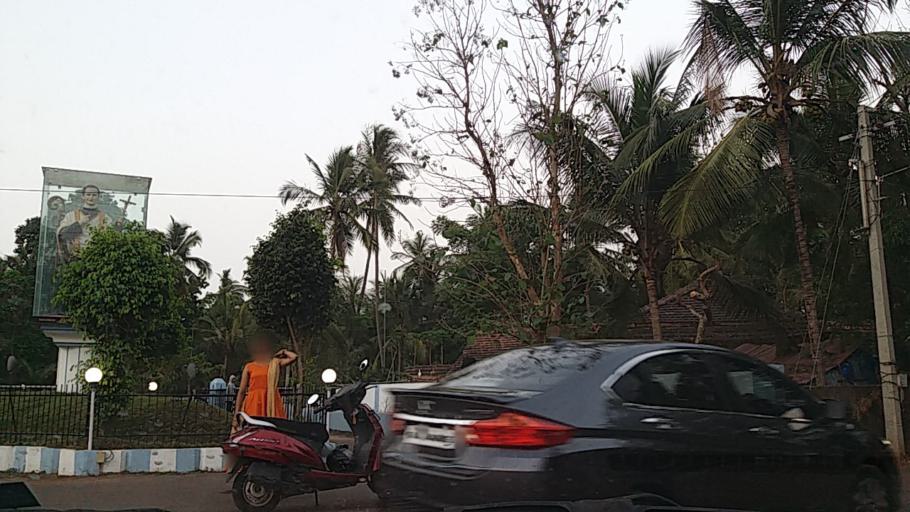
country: IN
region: Goa
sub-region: South Goa
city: Chinchinim
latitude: 15.2168
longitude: 73.9696
